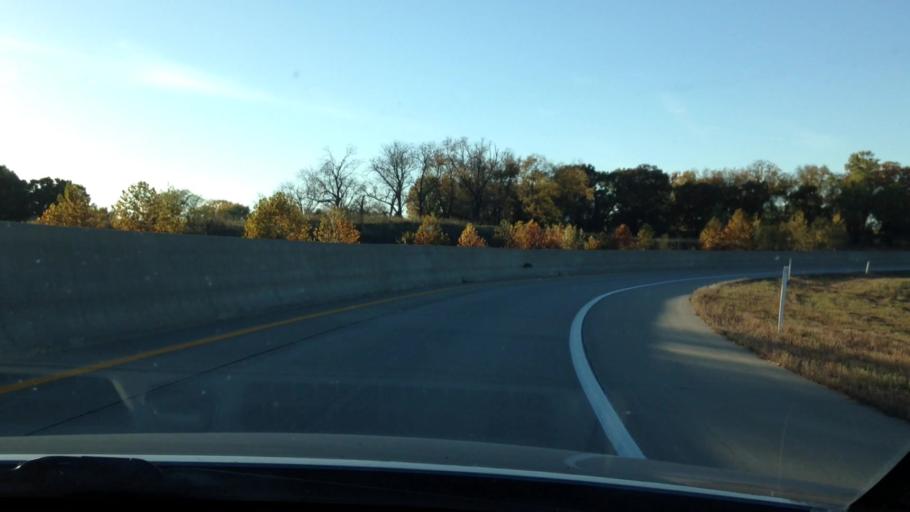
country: US
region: Kansas
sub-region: Leavenworth County
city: Basehor
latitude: 39.1139
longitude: -94.8955
